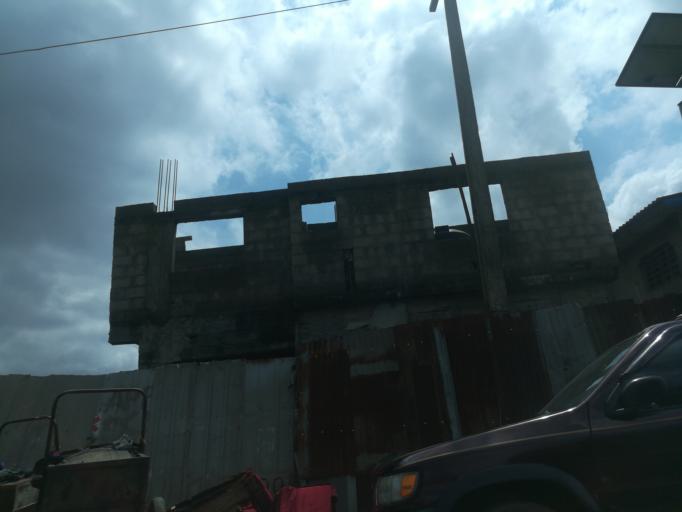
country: NG
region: Lagos
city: Somolu
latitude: 6.5374
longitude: 3.3641
